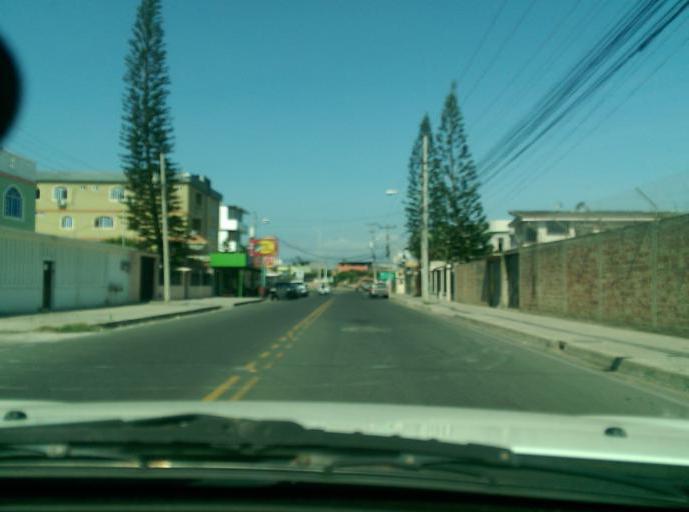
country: EC
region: Manabi
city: Manta
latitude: -0.9577
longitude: -80.7494
